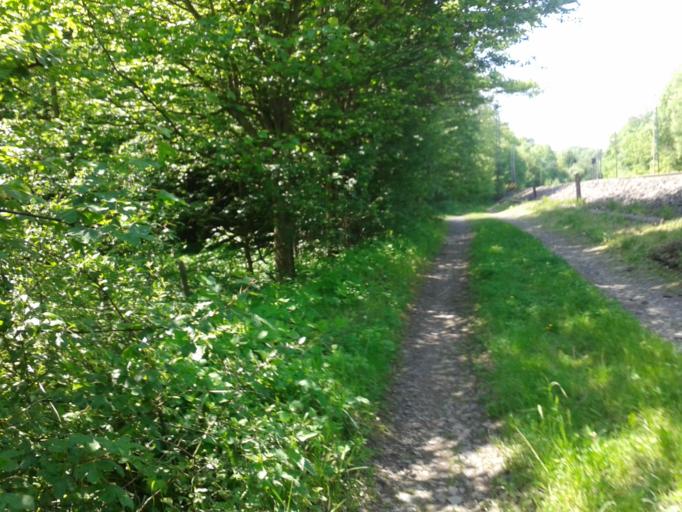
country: DE
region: Hesse
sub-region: Regierungsbezirk Darmstadt
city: Schluchtern
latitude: 50.3393
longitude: 9.5058
